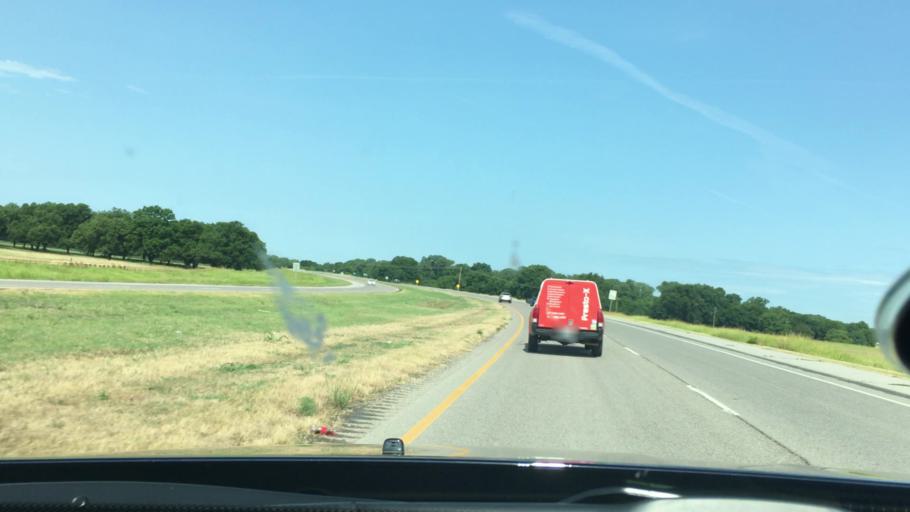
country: US
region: Oklahoma
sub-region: Murray County
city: Davis
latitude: 34.5042
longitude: -97.1329
